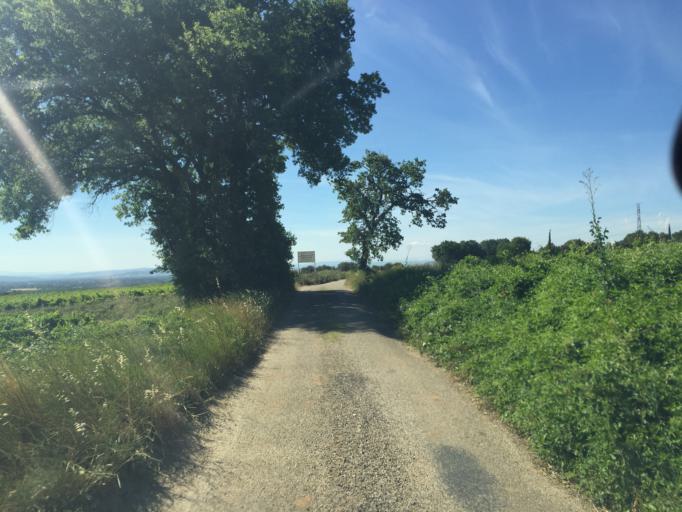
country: FR
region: Provence-Alpes-Cote d'Azur
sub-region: Departement du Vaucluse
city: Chateauneuf-du-Pape
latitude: 44.0855
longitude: 4.8057
